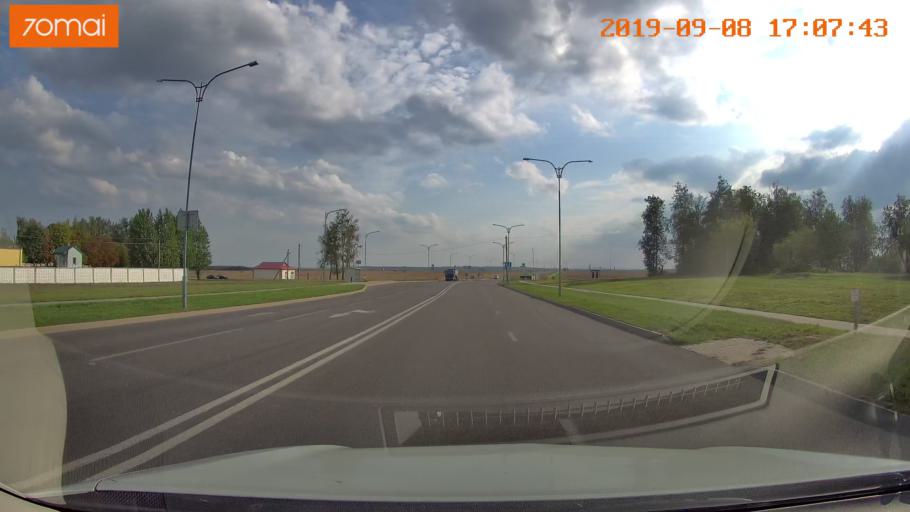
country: BY
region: Grodnenskaya
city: Hrodna
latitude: 53.6629
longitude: 23.9640
